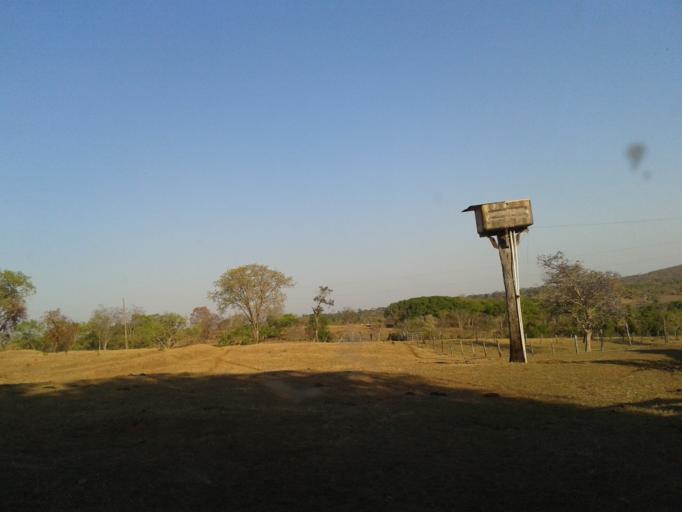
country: BR
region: Minas Gerais
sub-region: Campina Verde
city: Campina Verde
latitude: -19.2662
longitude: -49.6058
